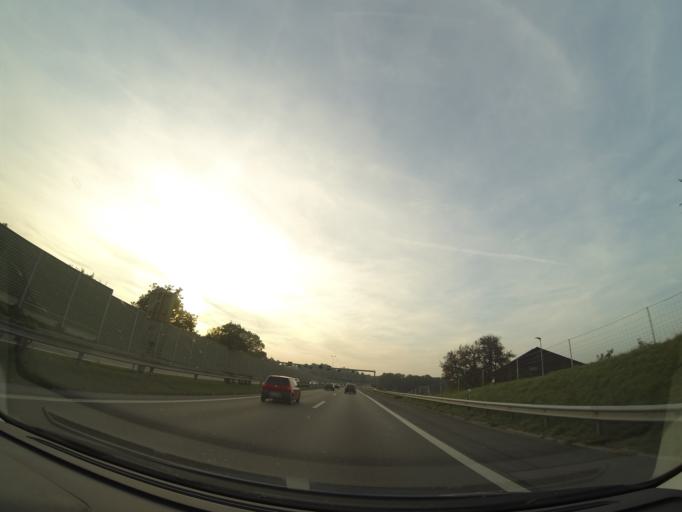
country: CH
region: Zurich
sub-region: Bezirk Horgen
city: Richterswil / Richterswil (Dorfkern)
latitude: 47.1959
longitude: 8.7089
